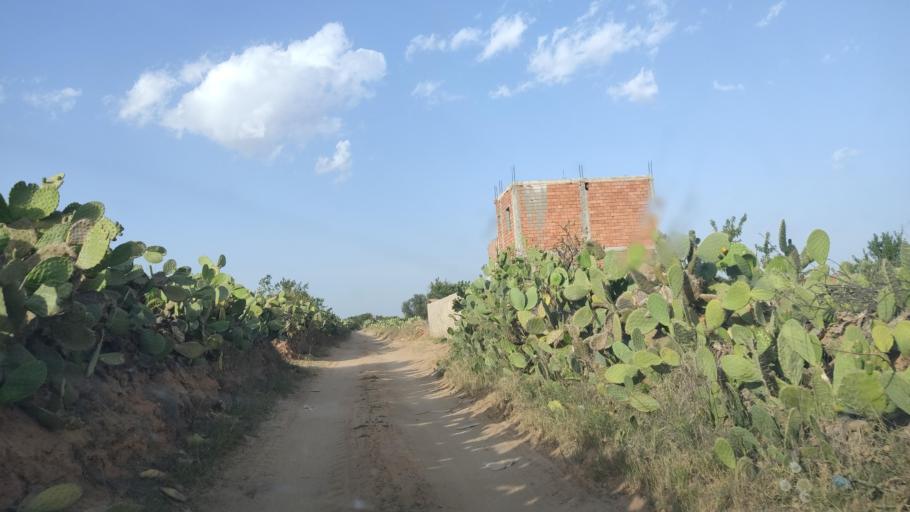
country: TN
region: Safaqis
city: Sfax
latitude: 34.8548
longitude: 10.5933
